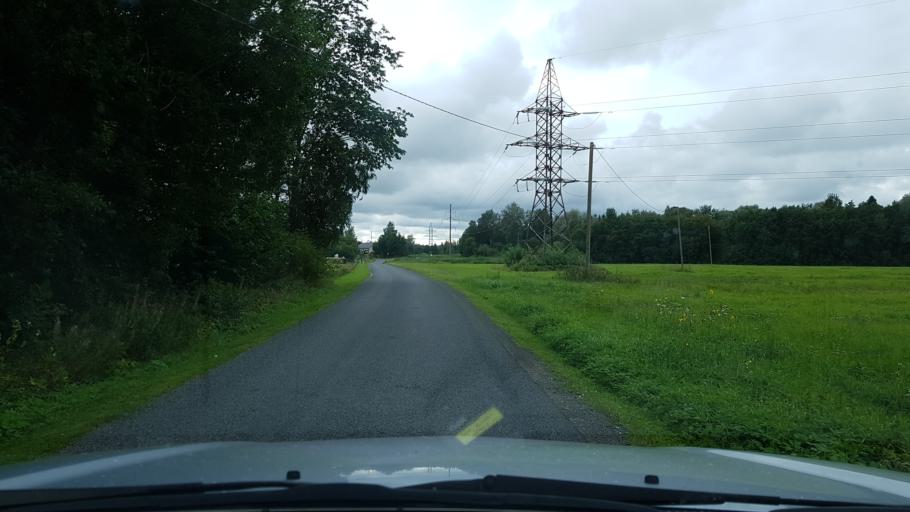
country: EE
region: Harju
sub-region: Joelaehtme vald
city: Loo
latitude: 59.3875
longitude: 24.9474
